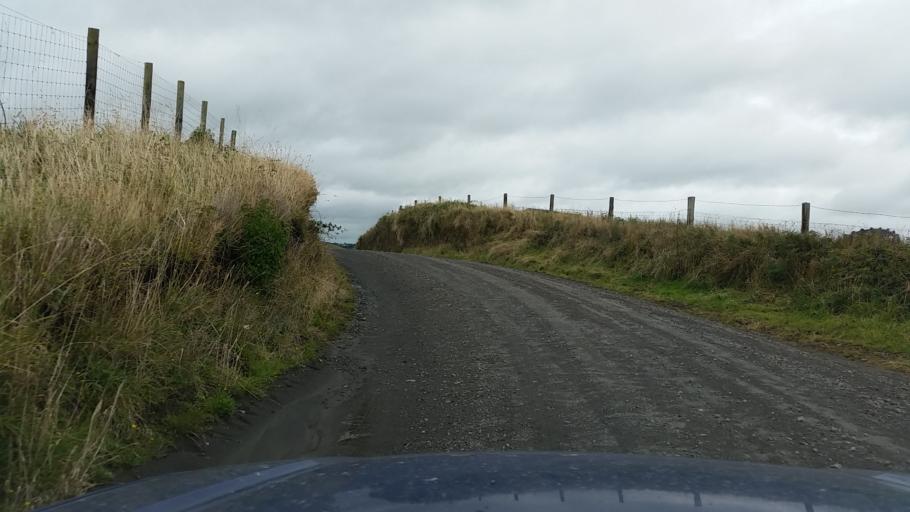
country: NZ
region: Taranaki
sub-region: South Taranaki District
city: Eltham
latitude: -39.2805
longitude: 174.3080
